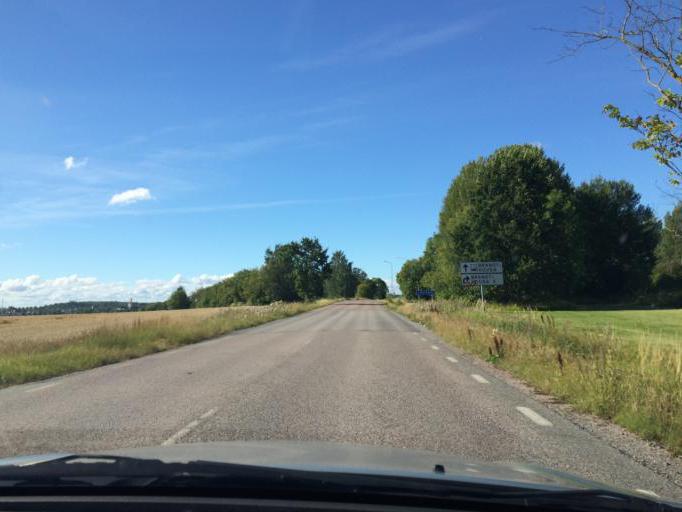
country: SE
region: Vaestmanland
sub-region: Vasteras
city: Hokasen
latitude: 59.6198
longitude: 16.6226
